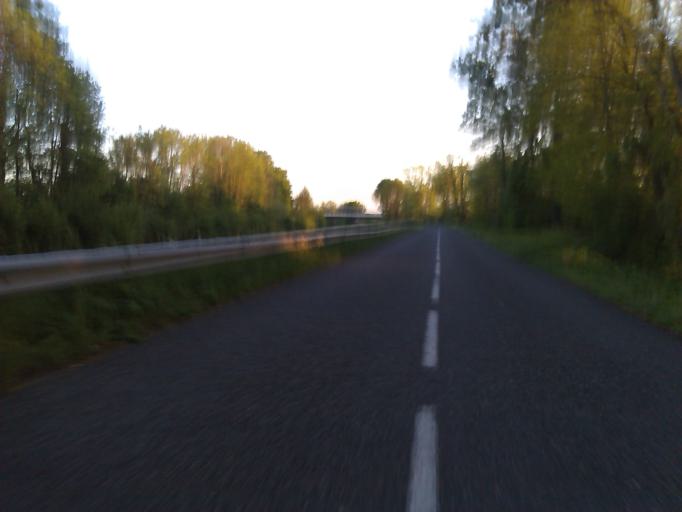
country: FR
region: Bourgogne
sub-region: Departement de Saone-et-Loire
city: Paray-le-Monial
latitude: 46.4604
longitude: 4.1605
